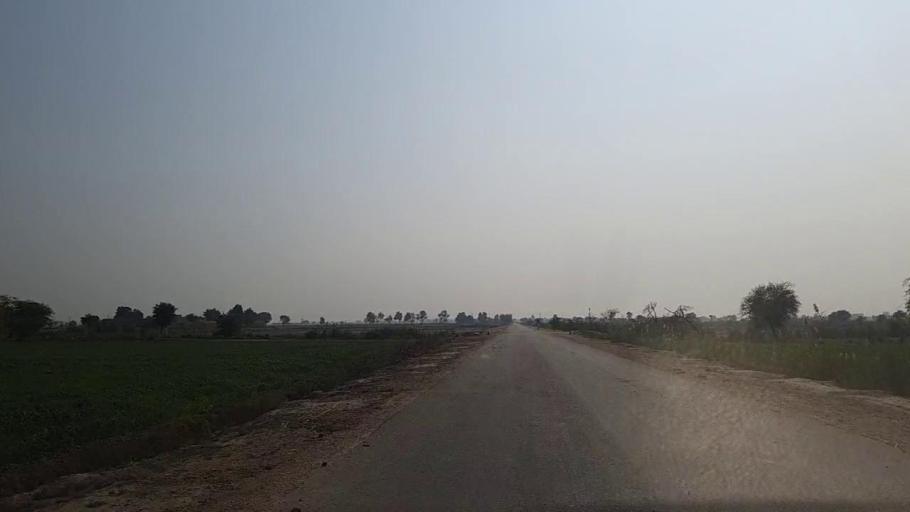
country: PK
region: Sindh
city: Jam Sahib
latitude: 26.3572
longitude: 68.5346
